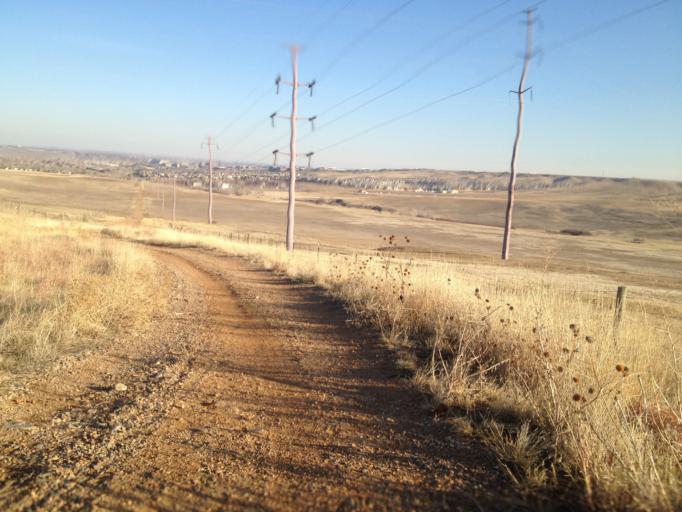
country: US
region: Colorado
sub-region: Boulder County
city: Superior
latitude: 39.9287
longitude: -105.1858
